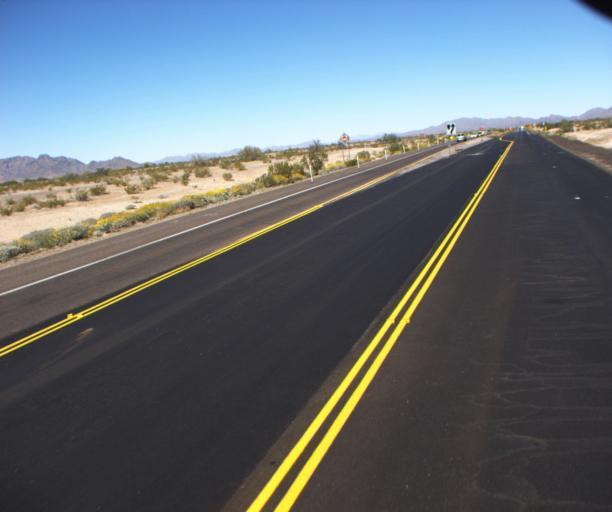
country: US
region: Arizona
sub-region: Maricopa County
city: Gila Bend
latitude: 32.9734
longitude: -112.6716
